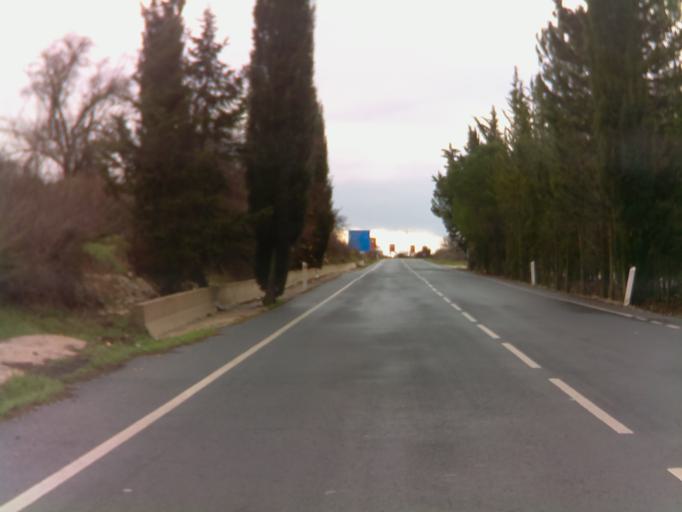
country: CY
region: Pafos
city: Pegeia
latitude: 34.9116
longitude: 32.4325
